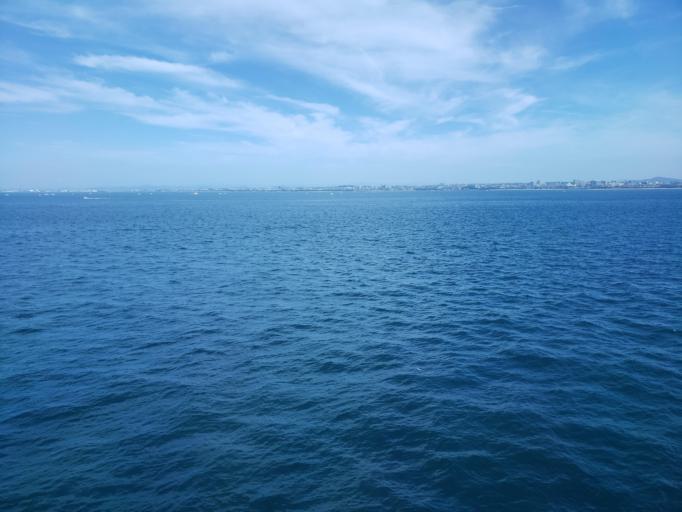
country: JP
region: Hyogo
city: Akashi
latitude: 34.6200
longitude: 134.9522
